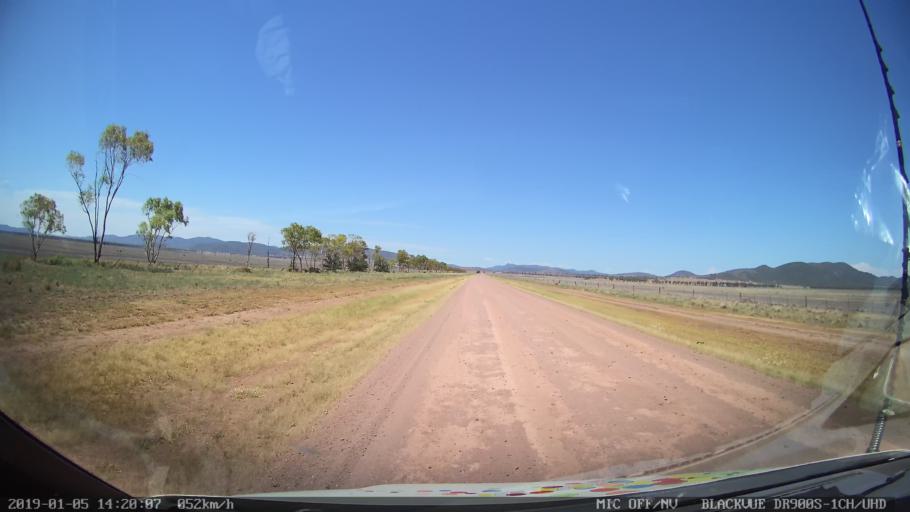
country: AU
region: New South Wales
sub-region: Liverpool Plains
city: Quirindi
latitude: -31.2492
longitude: 150.5022
